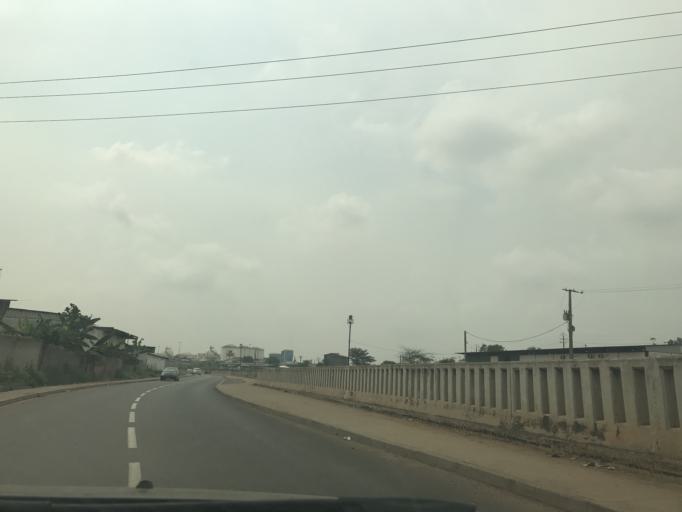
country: CM
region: Centre
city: Yaounde
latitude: 3.8385
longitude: 11.5128
